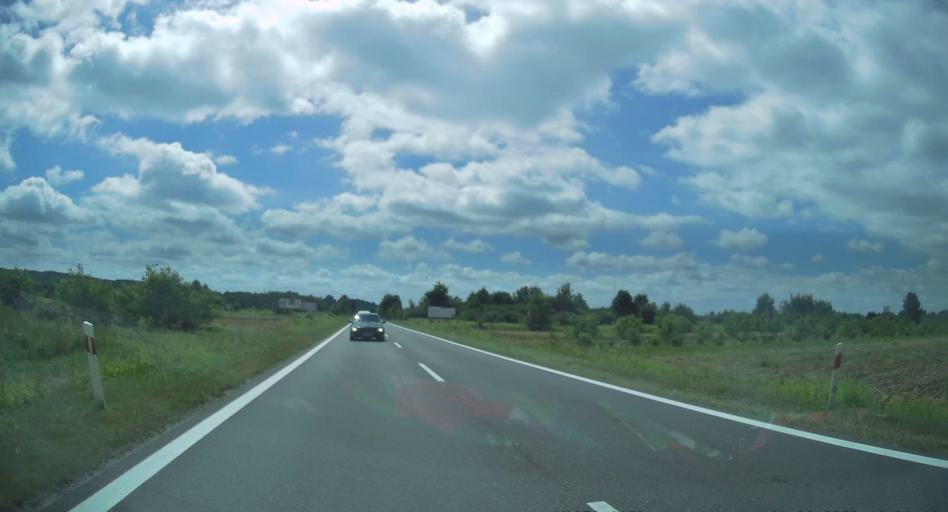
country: PL
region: Subcarpathian Voivodeship
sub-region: Powiat tarnobrzeski
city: Baranow Sandomierski
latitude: 50.5001
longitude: 21.5711
